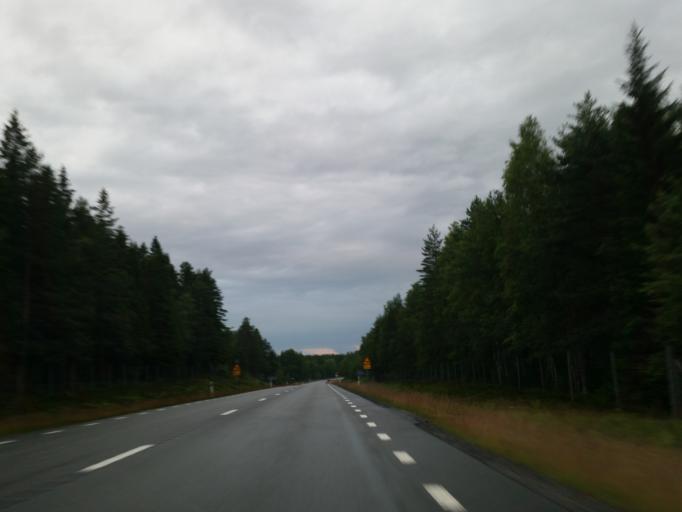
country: SE
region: Vaesterbotten
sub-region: Robertsfors Kommun
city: Robertsfors
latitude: 64.0296
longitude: 20.8416
